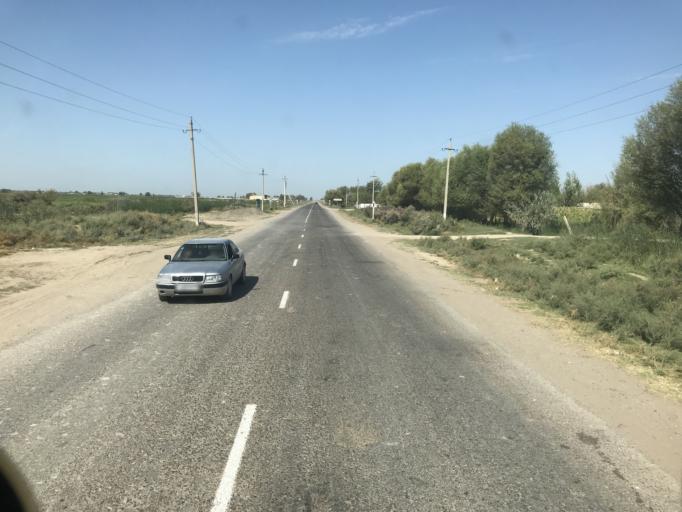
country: KZ
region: Ongtustik Qazaqstan
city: Myrzakent
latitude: 40.6854
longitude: 68.5713
